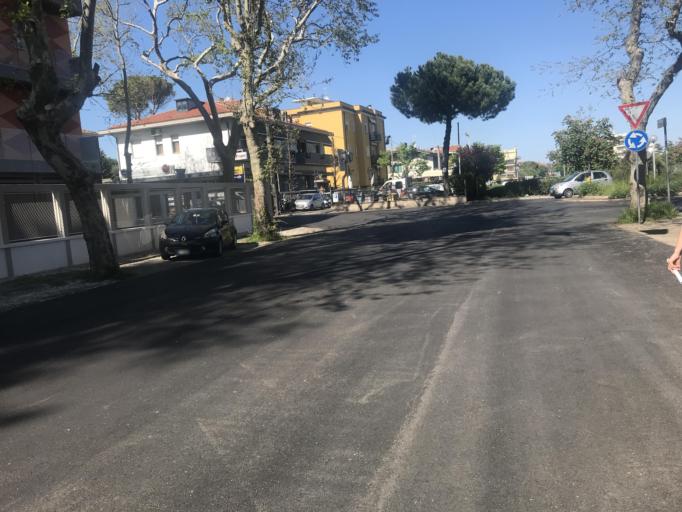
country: IT
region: Emilia-Romagna
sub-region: Provincia di Rimini
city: Rimini
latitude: 44.0541
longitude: 12.5773
